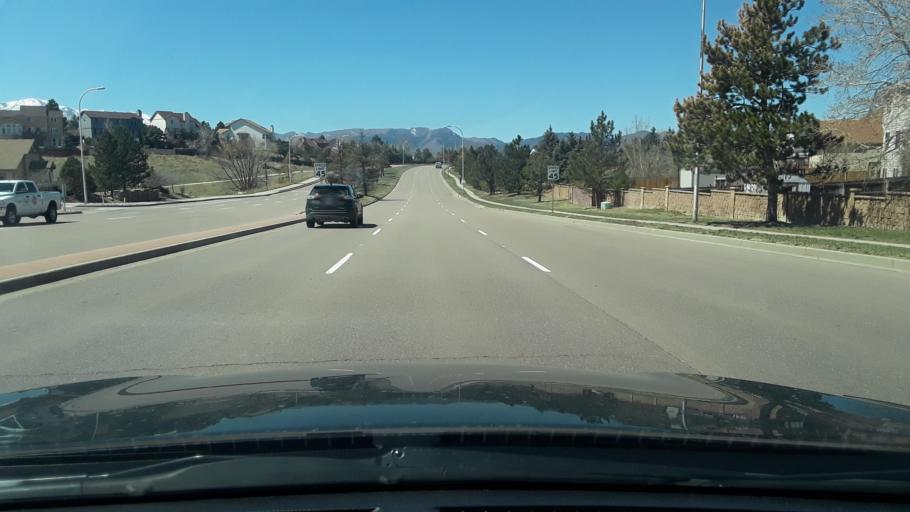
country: US
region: Colorado
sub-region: El Paso County
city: Black Forest
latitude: 38.9546
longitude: -104.7402
